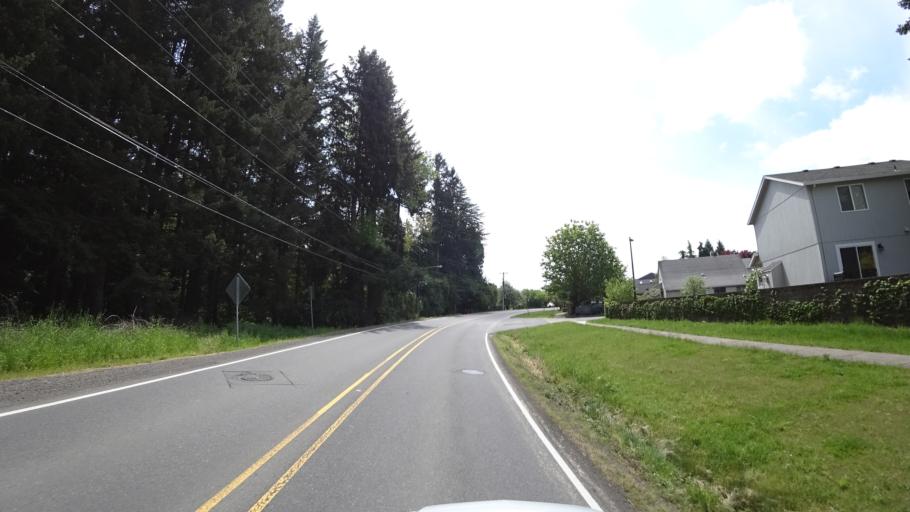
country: US
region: Oregon
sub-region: Washington County
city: Hillsboro
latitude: 45.5350
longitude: -122.9898
